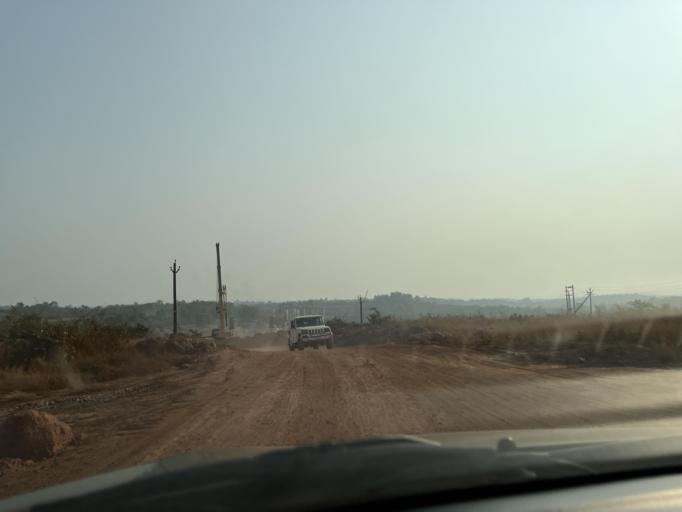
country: IN
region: Goa
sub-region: North Goa
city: Pernem
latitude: 15.6888
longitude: 73.8378
